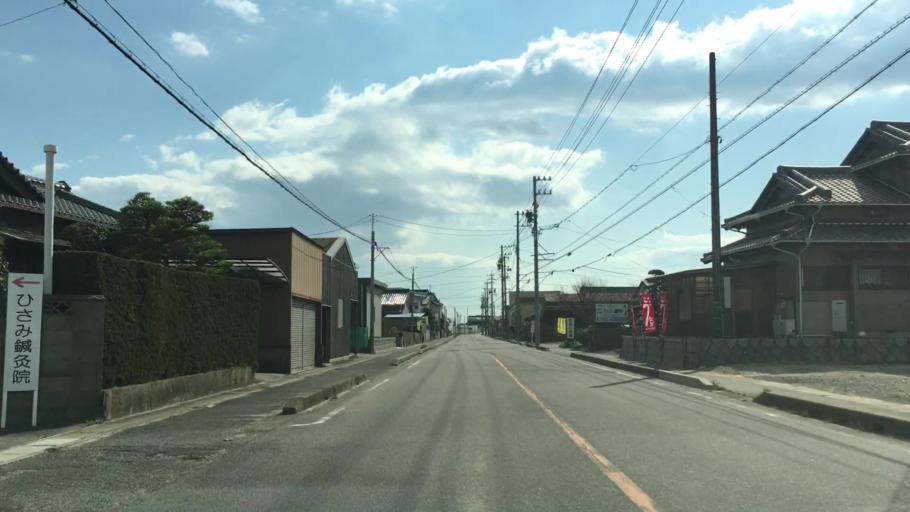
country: JP
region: Aichi
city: Ishiki
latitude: 34.7885
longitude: 137.0330
